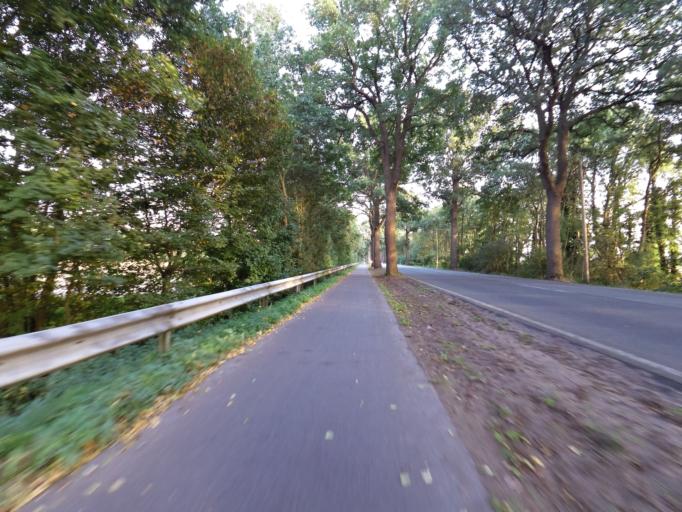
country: NL
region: Gelderland
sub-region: Gemeente Zevenaar
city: Zevenaar
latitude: 51.8981
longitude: 6.1376
